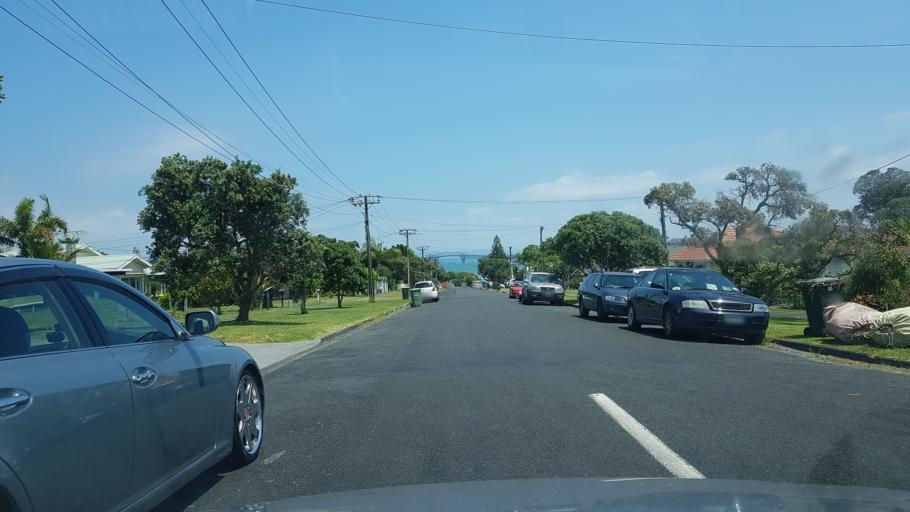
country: NZ
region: Auckland
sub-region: Auckland
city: North Shore
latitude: -36.8160
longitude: 174.7889
